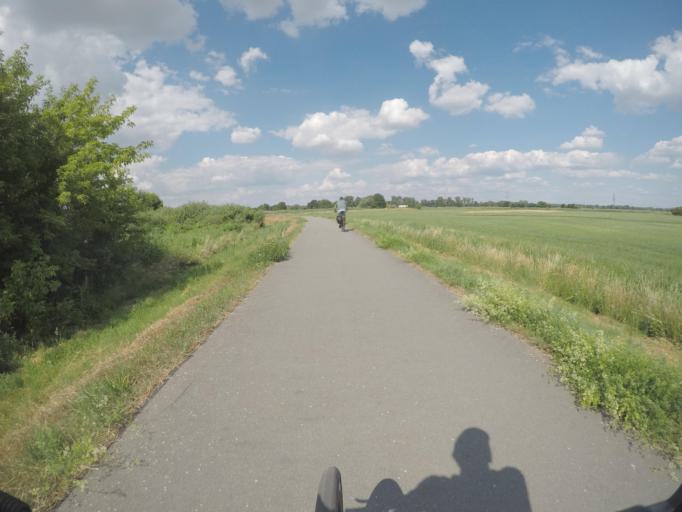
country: DE
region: Brandenburg
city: Ketzin
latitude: 52.4671
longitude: 12.8152
